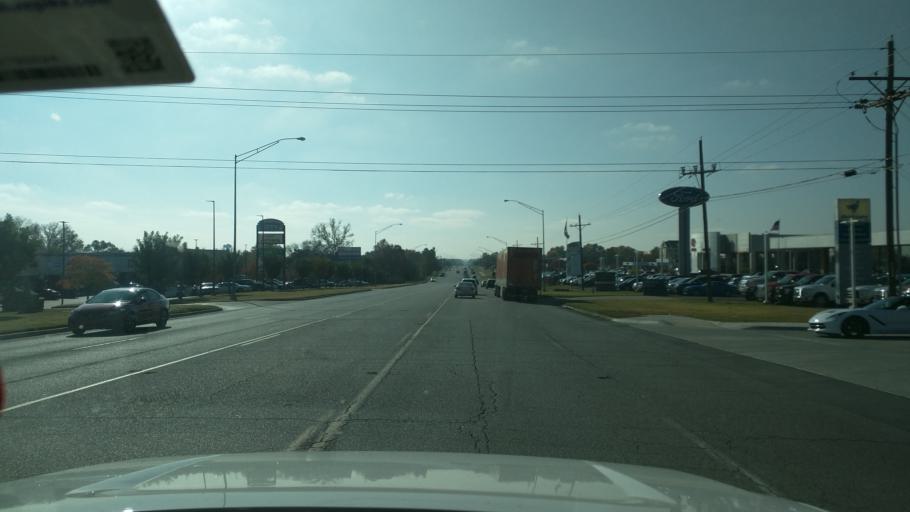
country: US
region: Oklahoma
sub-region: Washington County
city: Bartlesville
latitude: 36.7247
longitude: -95.9352
